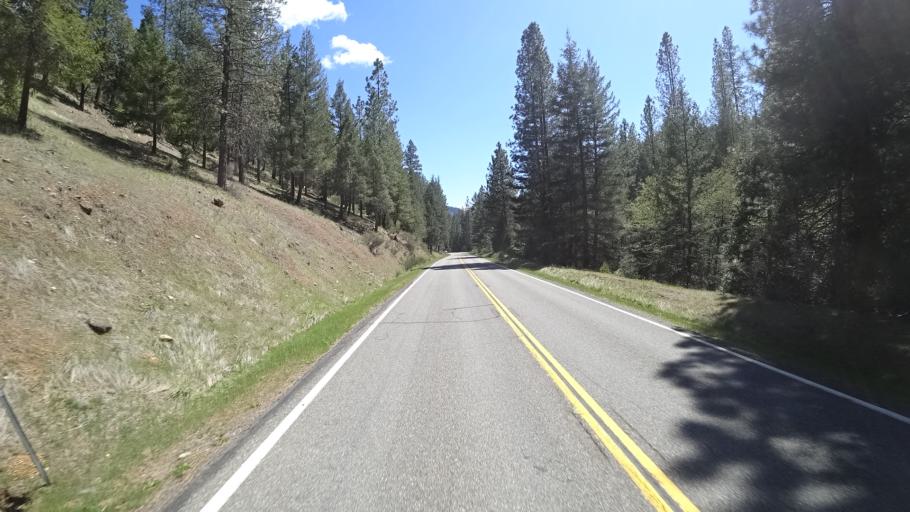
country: US
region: California
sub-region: Trinity County
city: Weaverville
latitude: 40.7681
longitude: -122.8899
